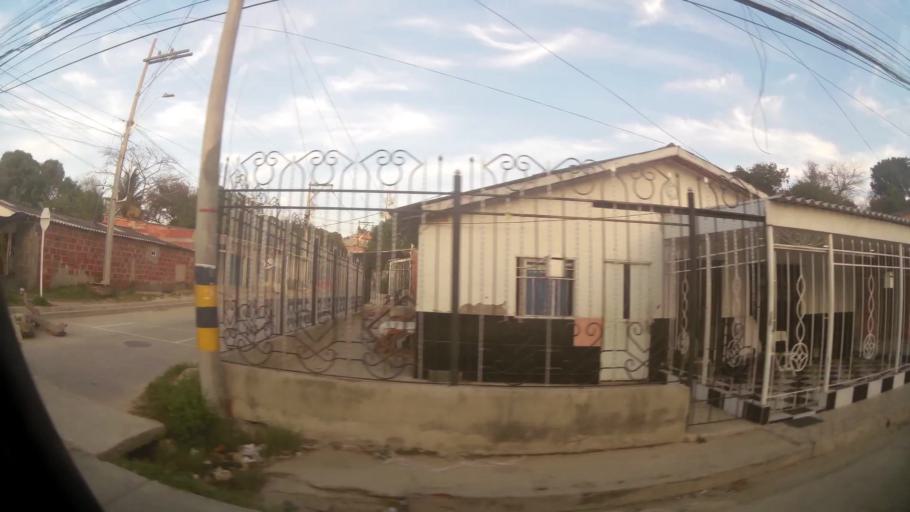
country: CO
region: Atlantico
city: Barranquilla
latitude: 10.9495
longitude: -74.8166
